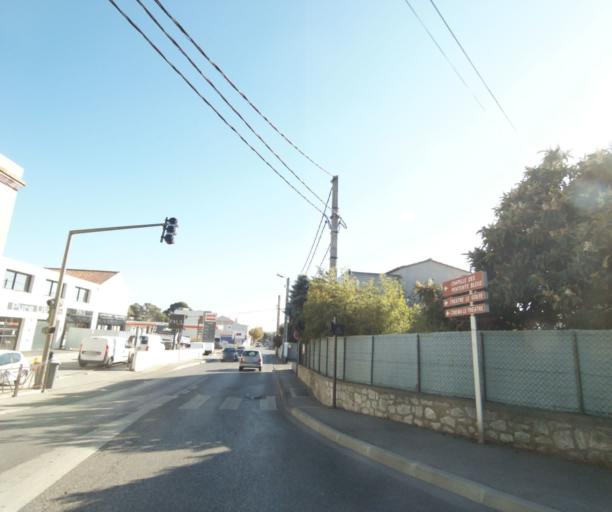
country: FR
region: Provence-Alpes-Cote d'Azur
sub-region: Departement des Bouches-du-Rhone
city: La Ciotat
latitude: 43.1857
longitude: 5.6078
